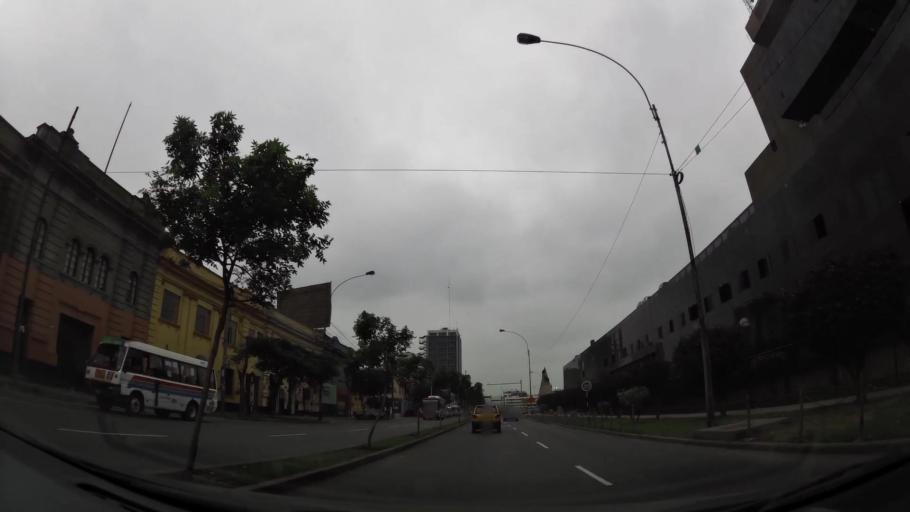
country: PE
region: Lima
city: Lima
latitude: -12.0647
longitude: -77.0410
